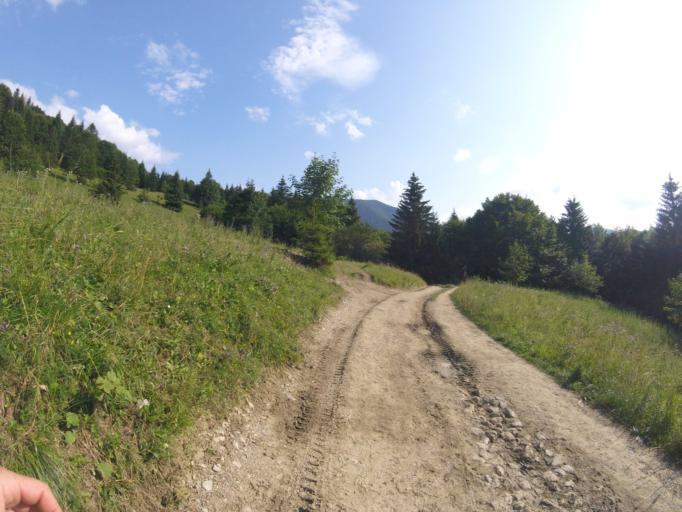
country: SK
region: Zilinsky
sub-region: Okres Zilina
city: Terchova
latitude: 49.2394
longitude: 19.0731
